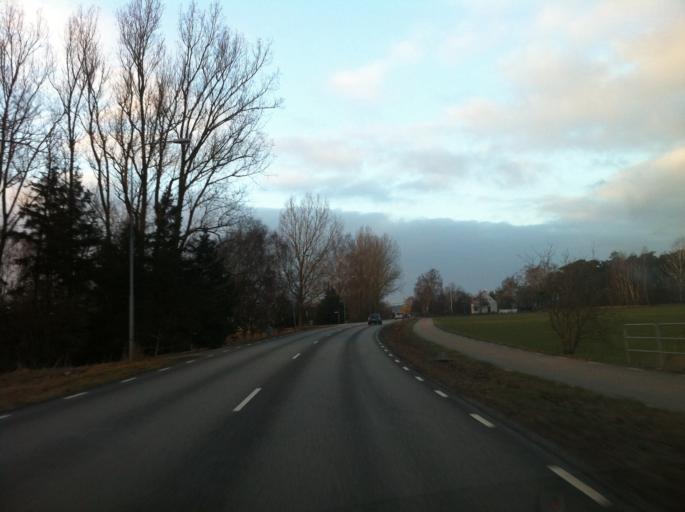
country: SE
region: Skane
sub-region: Kavlinge Kommun
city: Loddekopinge
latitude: 55.7783
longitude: 13.0079
